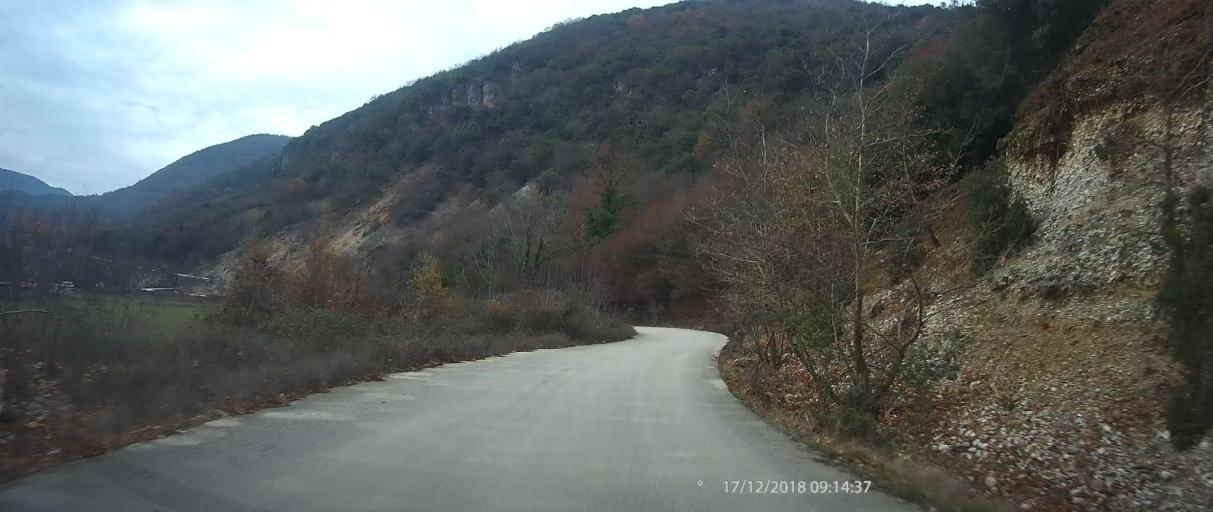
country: GR
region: Epirus
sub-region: Nomos Ioanninon
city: Kalpaki
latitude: 39.9716
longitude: 20.6549
